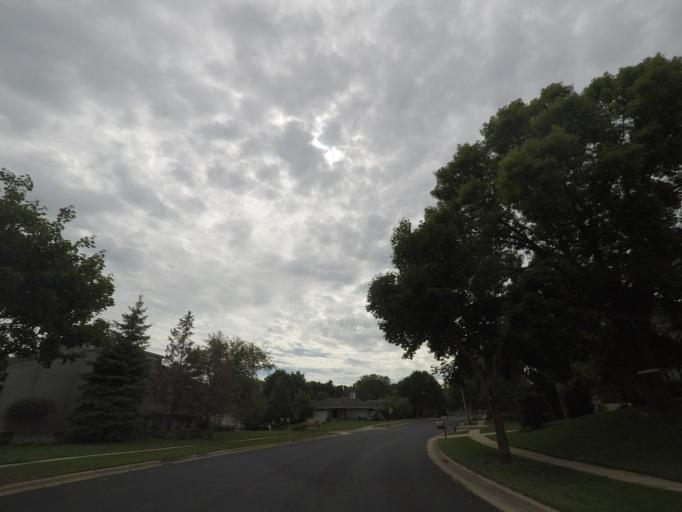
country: US
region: Wisconsin
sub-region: Dane County
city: Middleton
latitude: 43.0874
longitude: -89.4944
